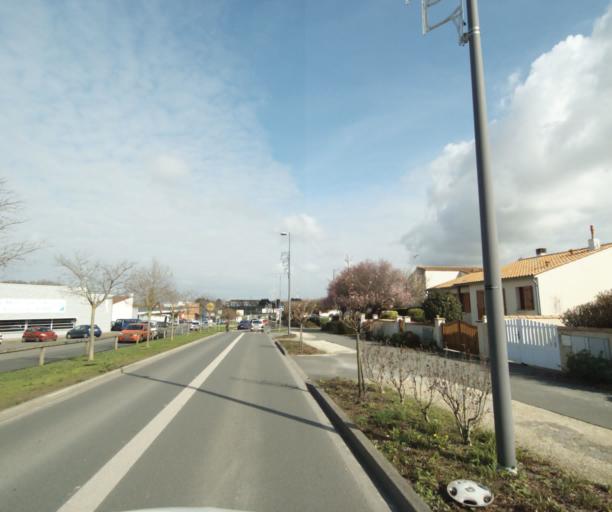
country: FR
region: Poitou-Charentes
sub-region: Departement de la Charente-Maritime
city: Lagord
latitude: 46.1776
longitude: -1.1556
